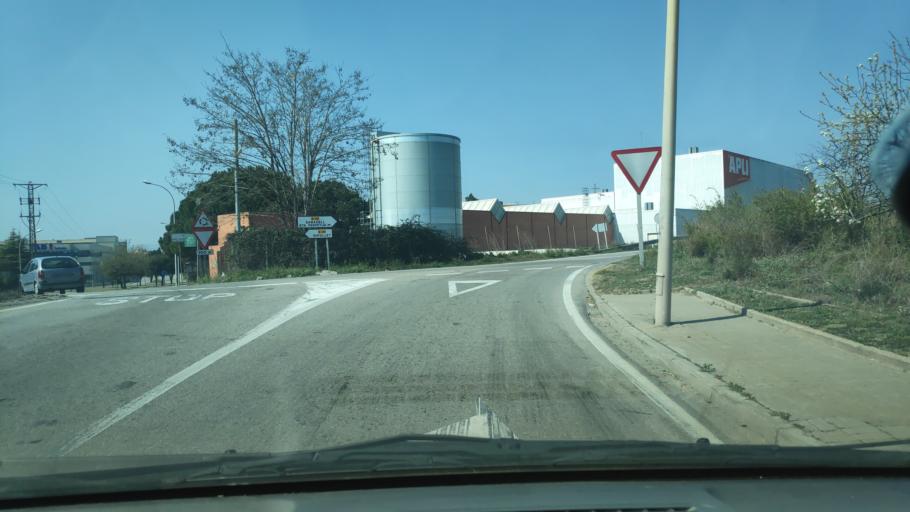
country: ES
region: Catalonia
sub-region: Provincia de Barcelona
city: Barbera del Valles
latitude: 41.5233
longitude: 2.1494
